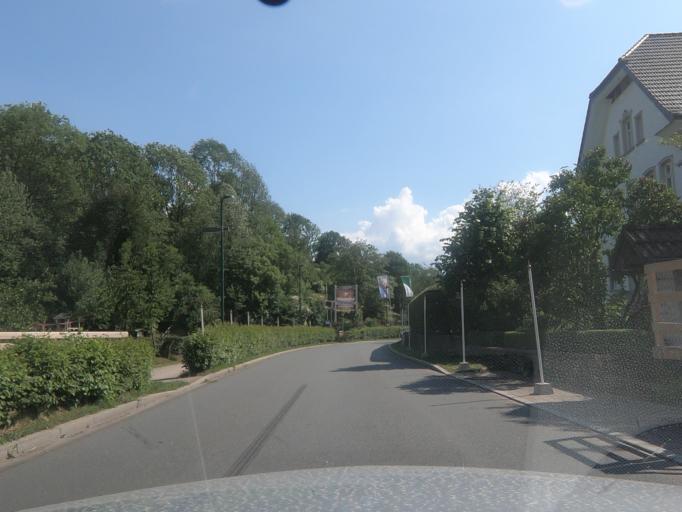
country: DE
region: North Rhine-Westphalia
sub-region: Regierungsbezirk Arnsberg
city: Finnentrop
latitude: 51.1220
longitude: 7.9738
